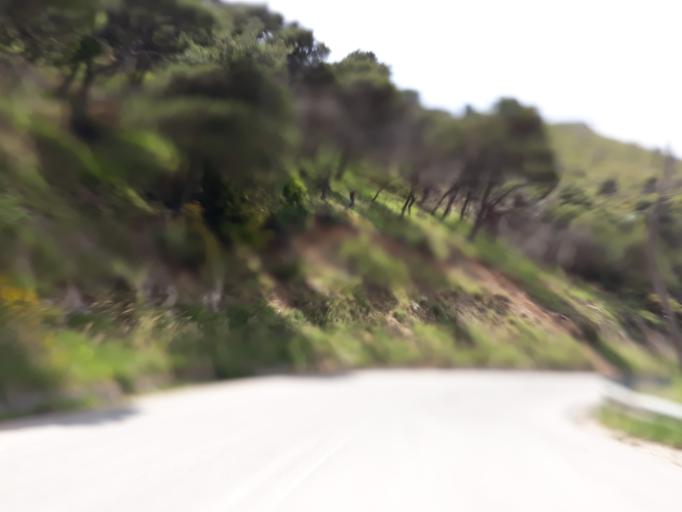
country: GR
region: Attica
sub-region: Nomarchia Dytikis Attikis
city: Magoula
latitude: 38.1648
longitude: 23.5437
